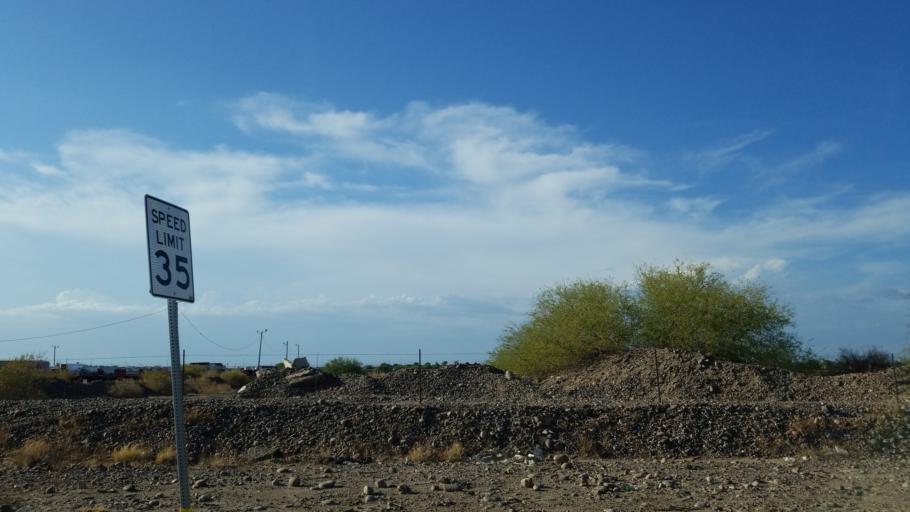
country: US
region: Arizona
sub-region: Maricopa County
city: Laveen
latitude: 33.3919
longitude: -112.2152
